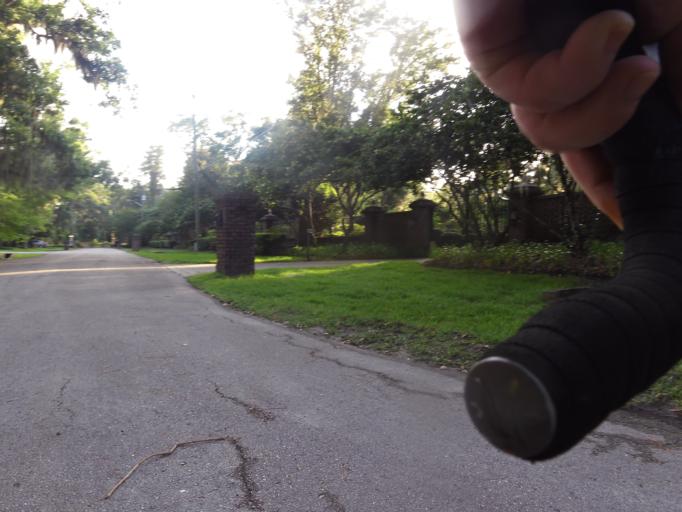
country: US
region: Florida
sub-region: Clay County
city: Orange Park
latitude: 30.2128
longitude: -81.6242
